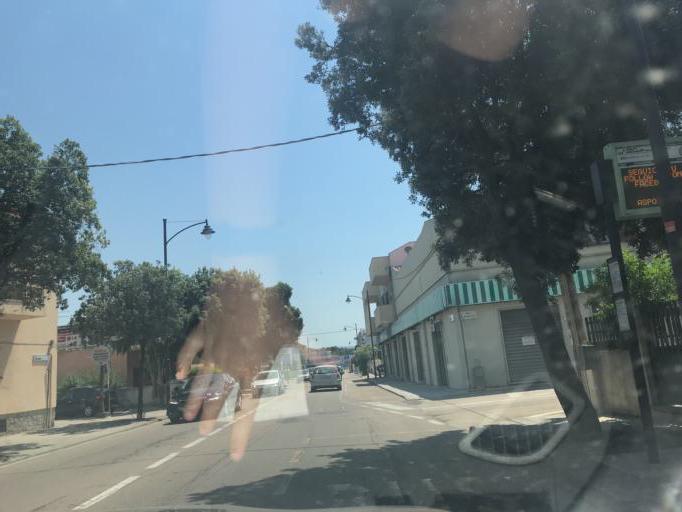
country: IT
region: Sardinia
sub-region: Provincia di Olbia-Tempio
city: Olbia
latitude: 40.9149
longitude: 9.5002
